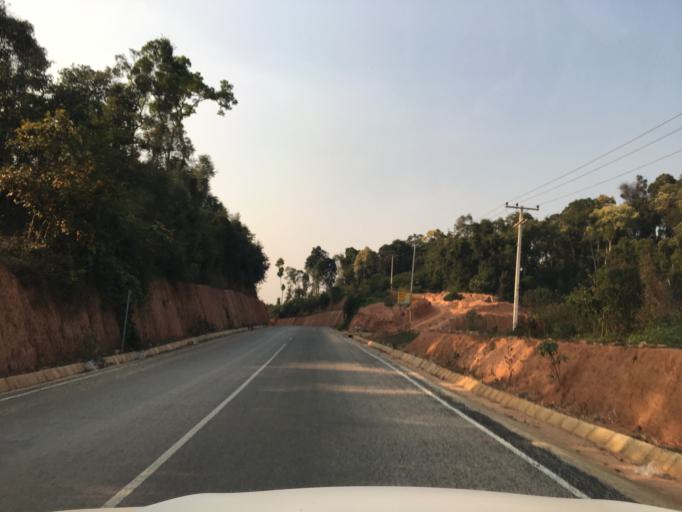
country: LA
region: Houaphan
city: Xam Nua
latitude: 20.6076
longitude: 104.0745
